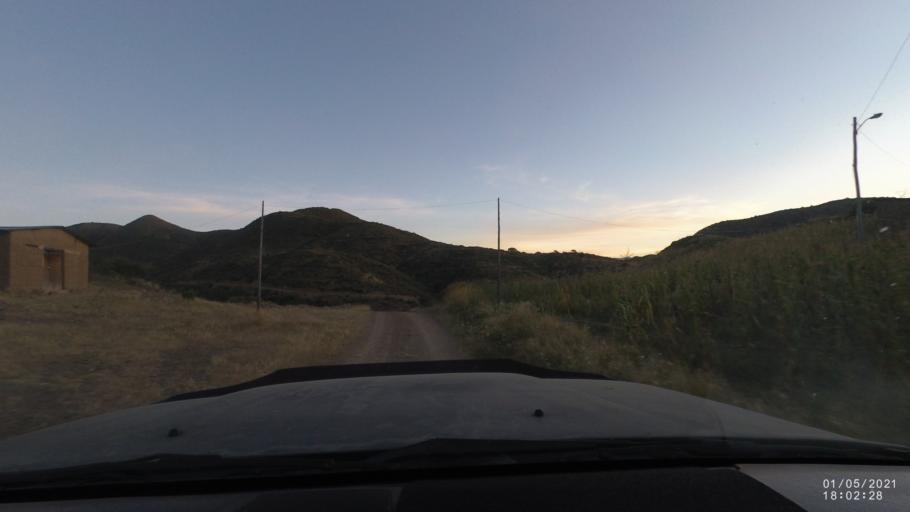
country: BO
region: Cochabamba
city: Capinota
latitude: -17.6878
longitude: -66.1740
